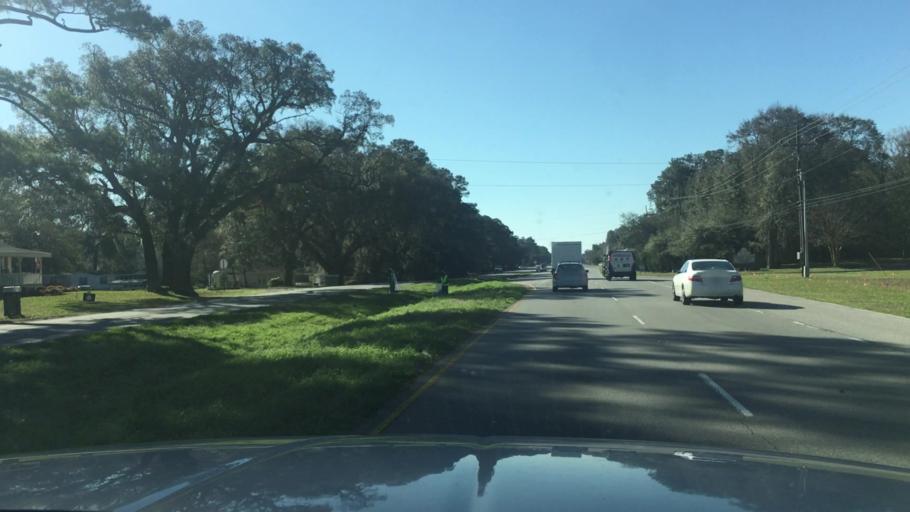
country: US
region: North Carolina
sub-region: New Hanover County
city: Sea Breeze
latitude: 34.0937
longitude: -77.8975
